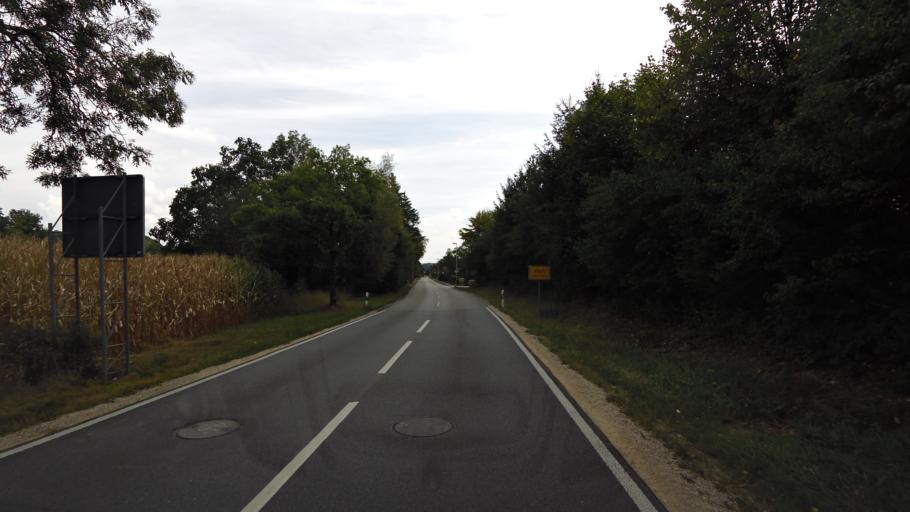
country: DE
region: Bavaria
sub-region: Upper Bavaria
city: Unterneukirchen
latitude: 48.1515
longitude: 12.6140
